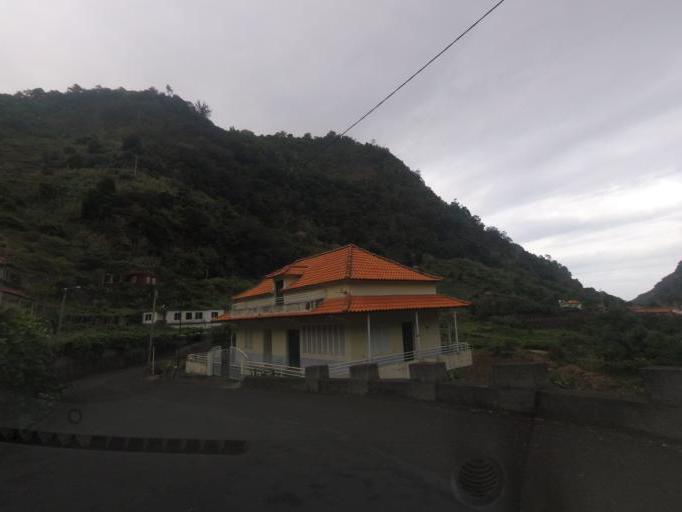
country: PT
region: Madeira
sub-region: Santana
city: Santana
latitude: 32.8181
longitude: -16.8997
